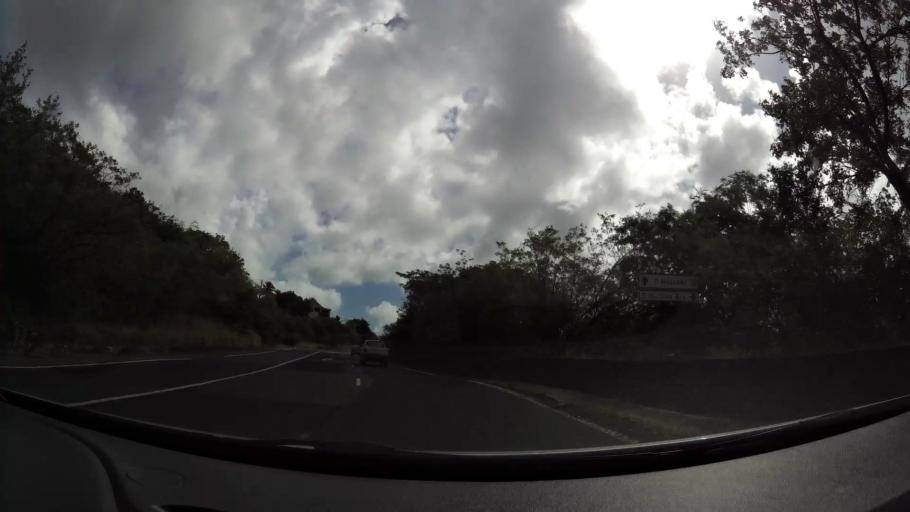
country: MQ
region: Martinique
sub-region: Martinique
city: Les Trois-Ilets
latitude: 14.4821
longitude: -61.0059
